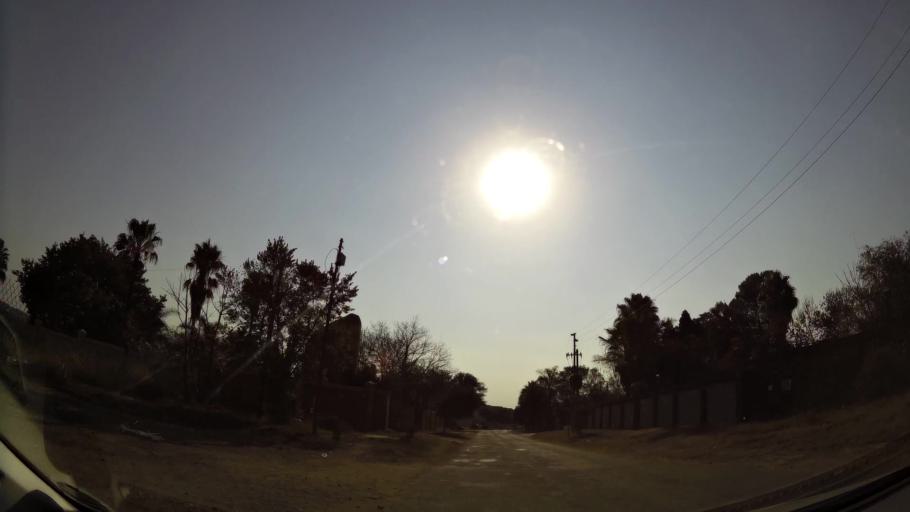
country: ZA
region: Gauteng
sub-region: City of Tshwane Metropolitan Municipality
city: Pretoria
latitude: -25.7618
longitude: 28.3298
